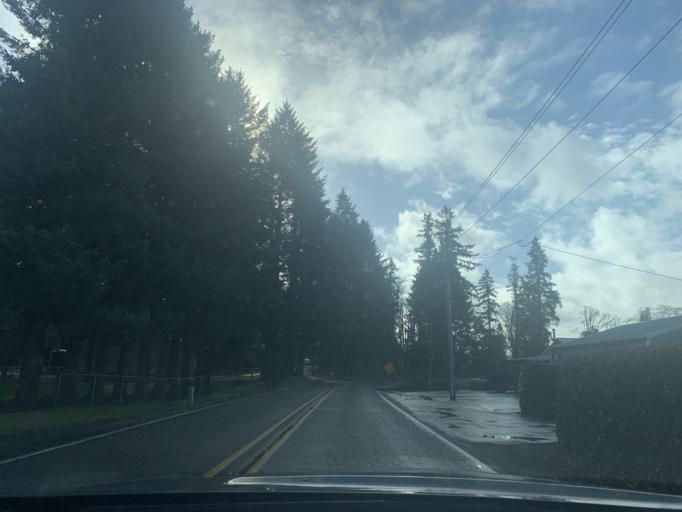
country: US
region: Oregon
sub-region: Washington County
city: Sherwood
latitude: 45.3911
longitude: -122.8459
